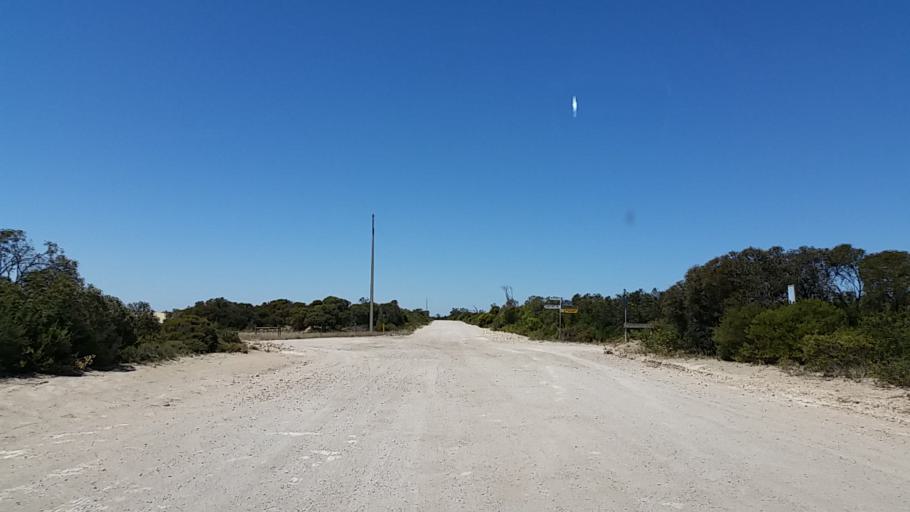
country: AU
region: South Australia
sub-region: Yorke Peninsula
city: Honiton
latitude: -35.1059
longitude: 137.4007
